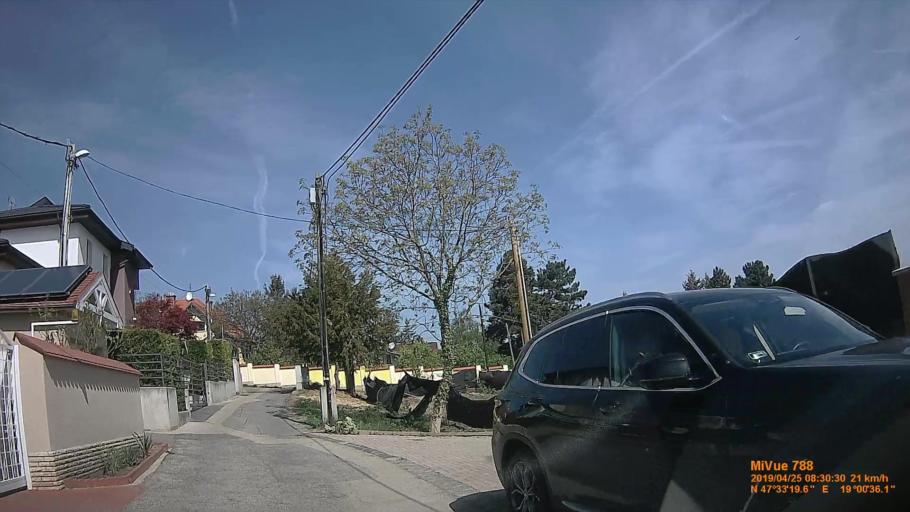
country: HU
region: Budapest
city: Budapest III. keruelet
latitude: 47.5555
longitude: 19.0099
